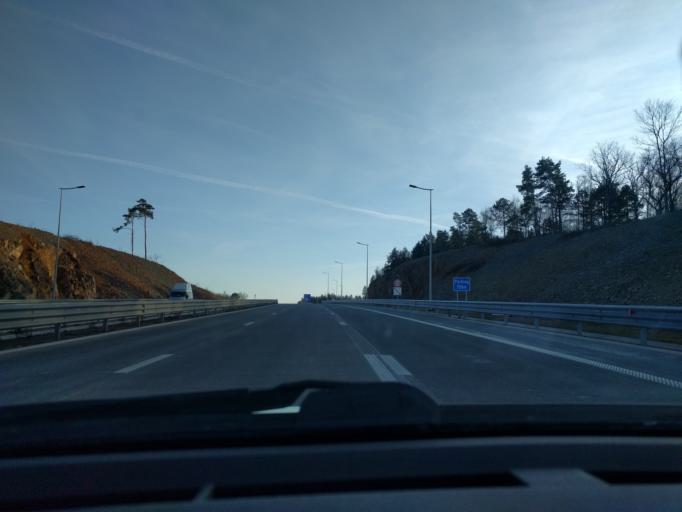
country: BE
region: Wallonia
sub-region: Province de Namur
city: Couvin
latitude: 50.0652
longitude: 4.5047
